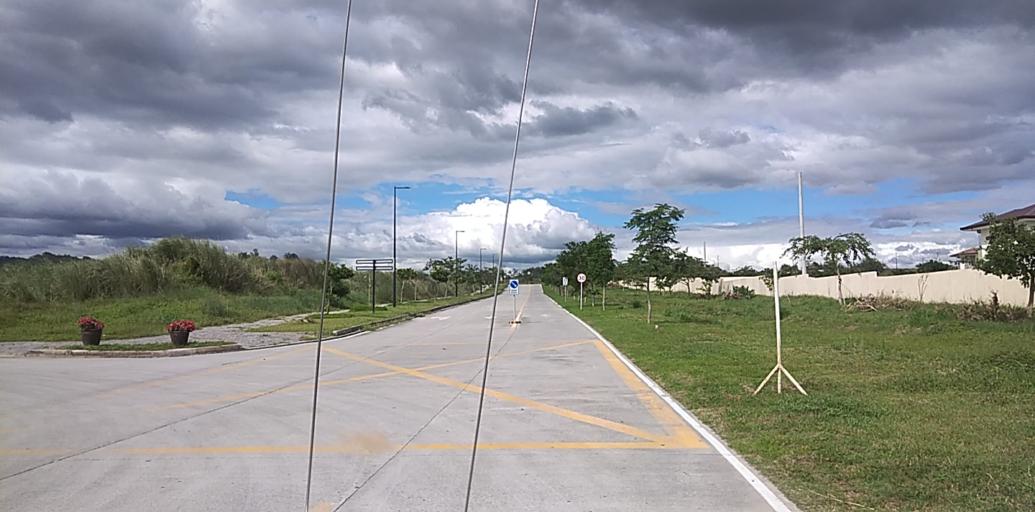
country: PH
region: Central Luzon
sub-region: Province of Pampanga
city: Dolores
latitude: 15.1136
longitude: 120.5130
